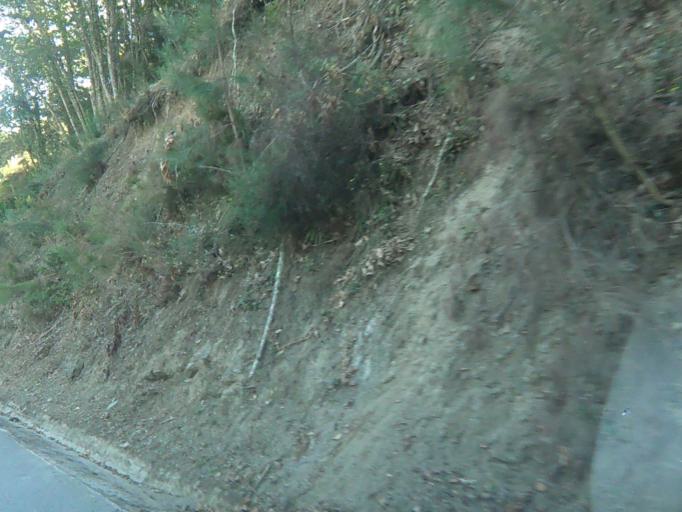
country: PT
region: Vila Real
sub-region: Santa Marta de Penaguiao
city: Santa Marta de Penaguiao
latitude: 41.2439
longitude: -7.8132
